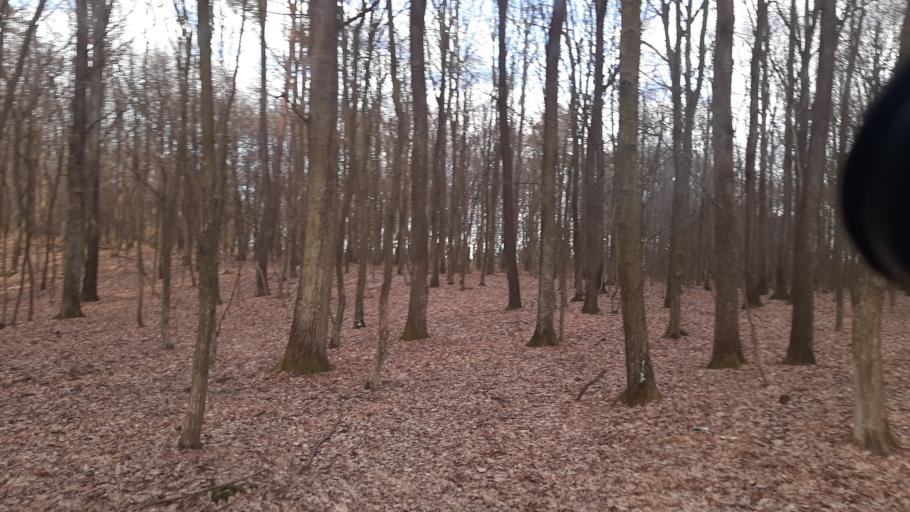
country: PL
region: Lublin Voivodeship
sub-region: Powiat lubelski
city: Jastkow
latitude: 51.3755
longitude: 22.4107
